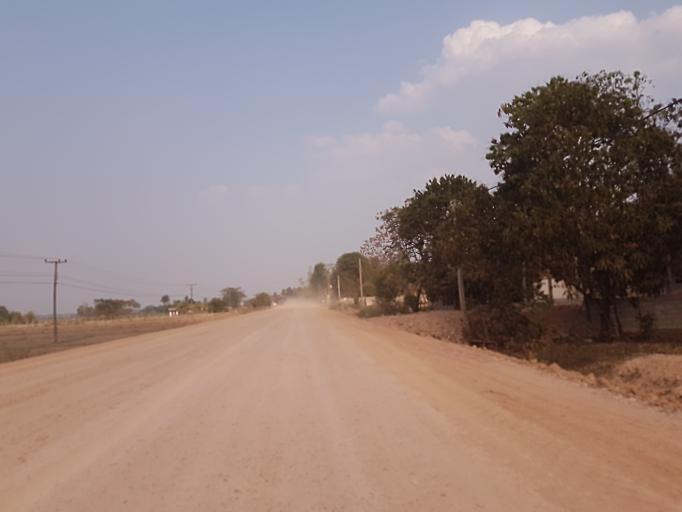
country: TH
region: Nong Khai
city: Nong Khai
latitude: 17.9811
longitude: 102.8845
